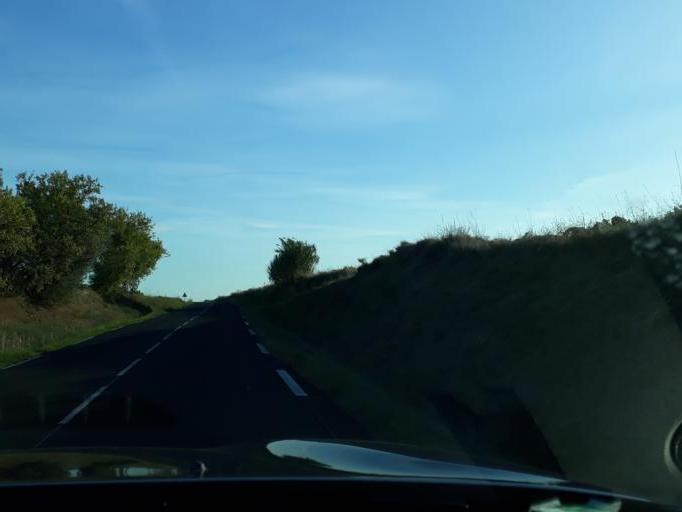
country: FR
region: Languedoc-Roussillon
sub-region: Departement de l'Herault
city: Pinet
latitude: 43.4154
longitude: 3.4893
